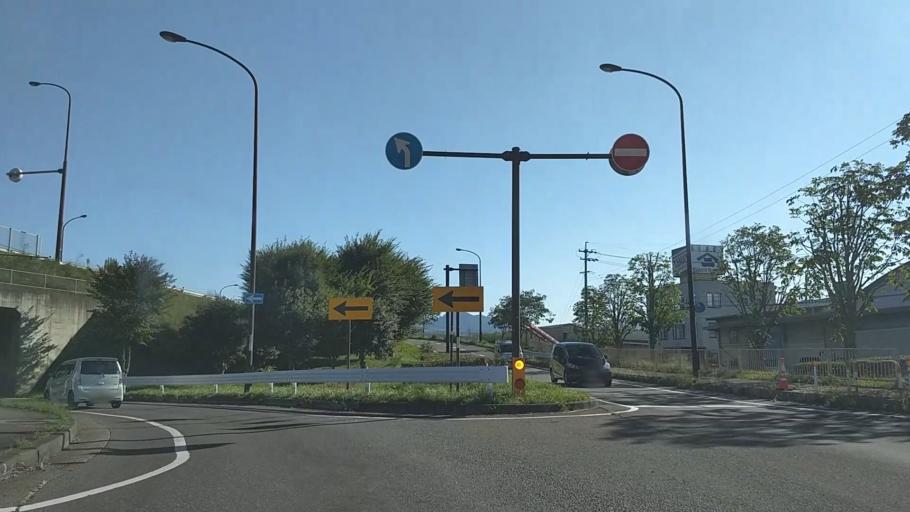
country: JP
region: Nagano
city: Nagano-shi
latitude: 36.5625
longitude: 138.1384
